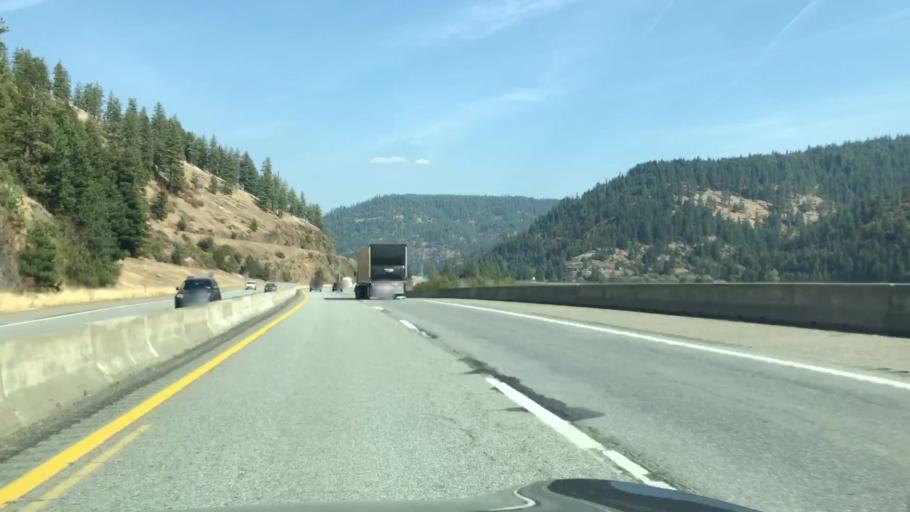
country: US
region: Idaho
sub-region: Kootenai County
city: Coeur d'Alene
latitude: 47.6235
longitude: -116.6604
